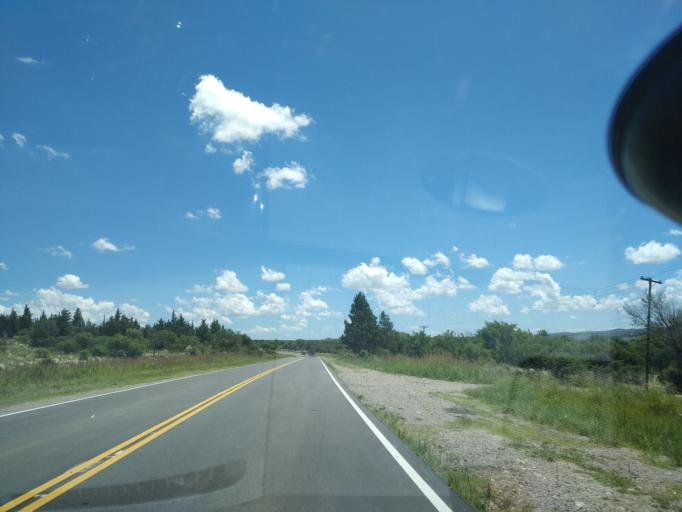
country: AR
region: Cordoba
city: Salsacate
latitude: -31.3524
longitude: -65.0970
